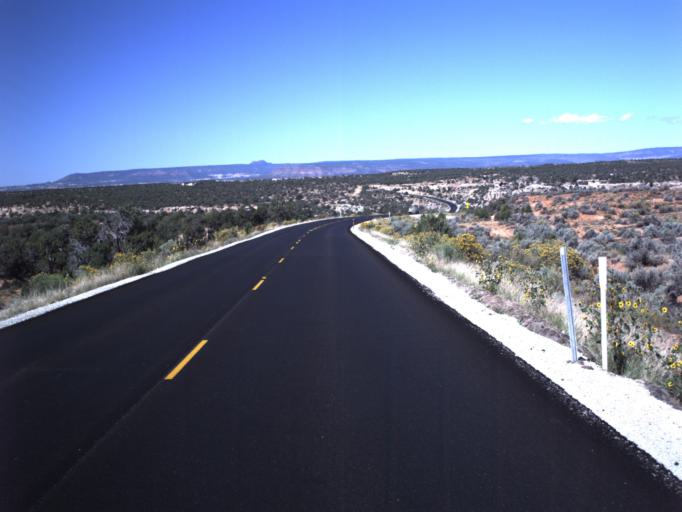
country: US
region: Utah
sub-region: San Juan County
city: Blanding
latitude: 37.5740
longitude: -109.4997
